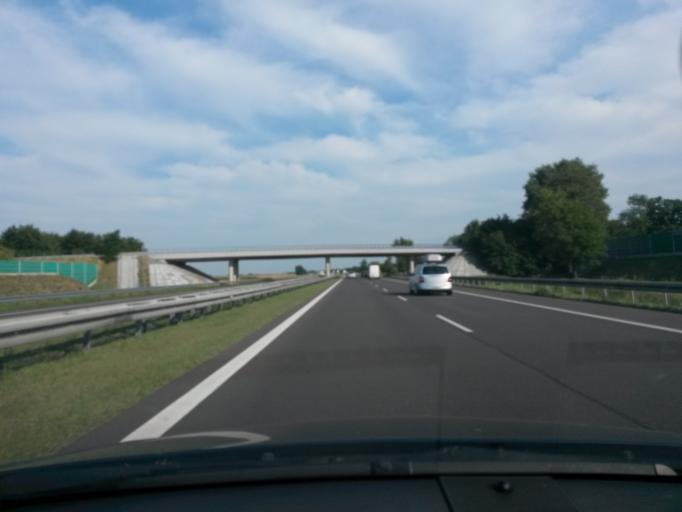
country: PL
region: Greater Poland Voivodeship
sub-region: Powiat slupecki
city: Ladek
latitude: 52.2371
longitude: 17.8886
